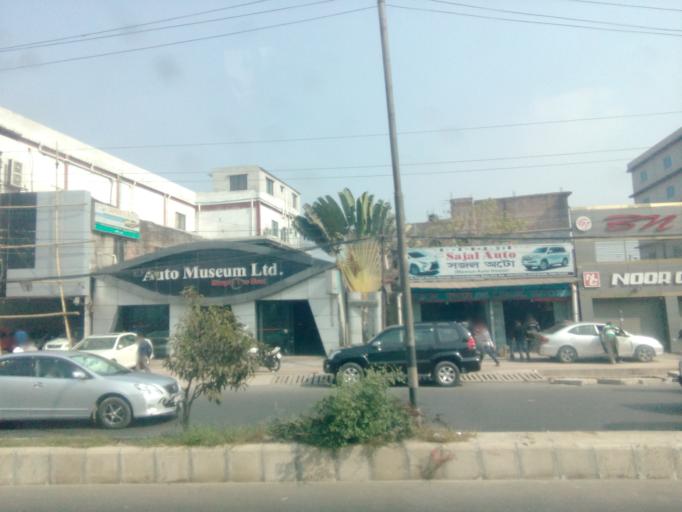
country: BD
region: Dhaka
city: Paltan
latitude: 23.8051
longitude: 90.4220
